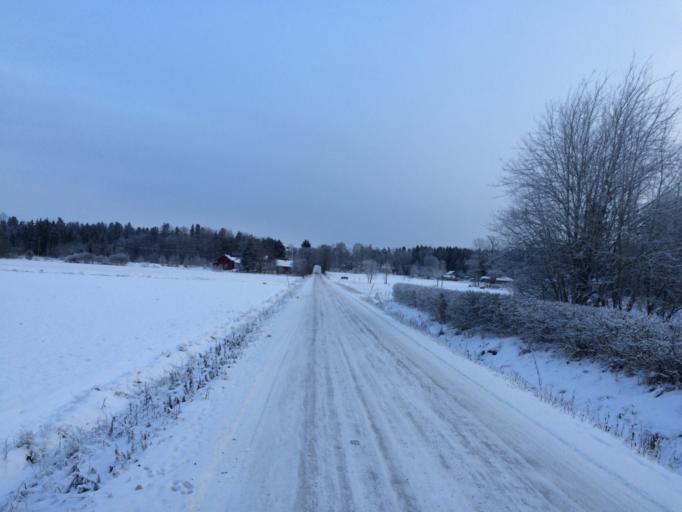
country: SE
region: Uppsala
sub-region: Enkopings Kommun
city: Orsundsbro
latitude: 59.9085
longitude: 17.2011
